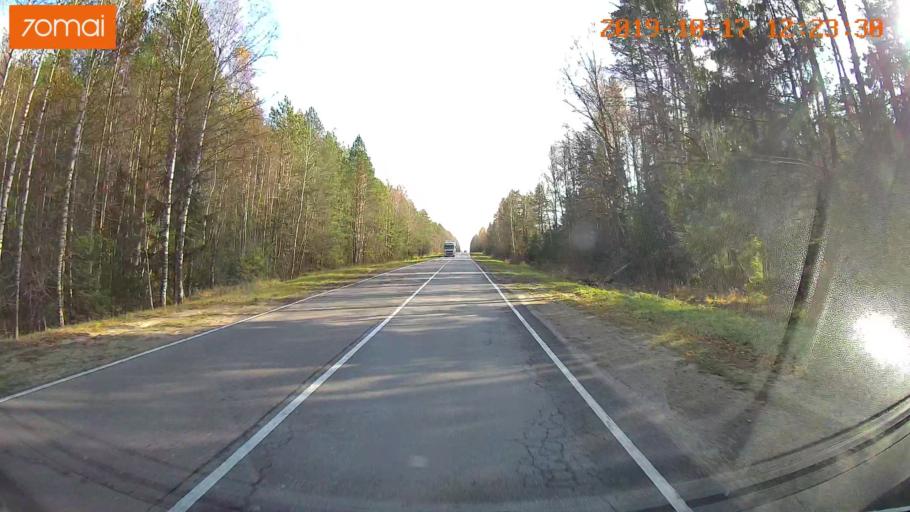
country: RU
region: Rjazan
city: Gus'-Zheleznyy
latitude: 55.0434
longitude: 41.1949
